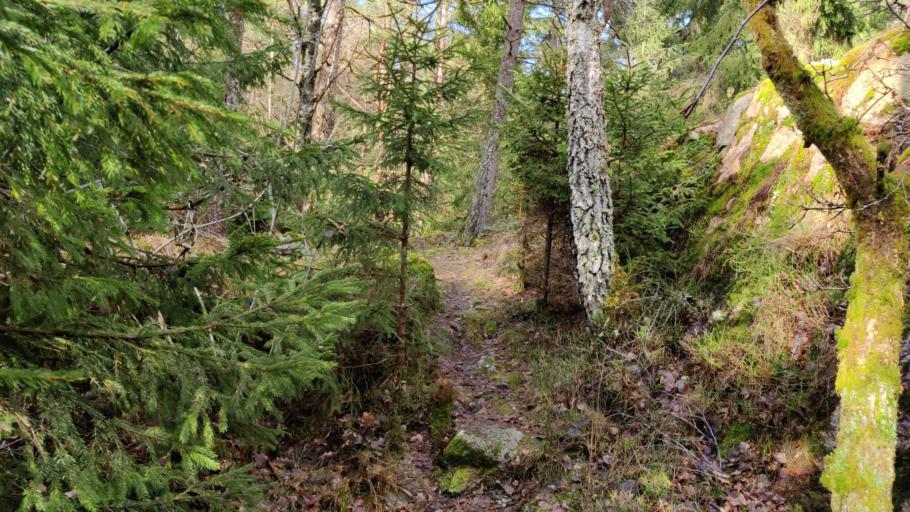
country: SE
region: Vaestra Goetaland
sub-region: Uddevalla Kommun
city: Uddevalla
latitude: 58.3477
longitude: 11.9690
